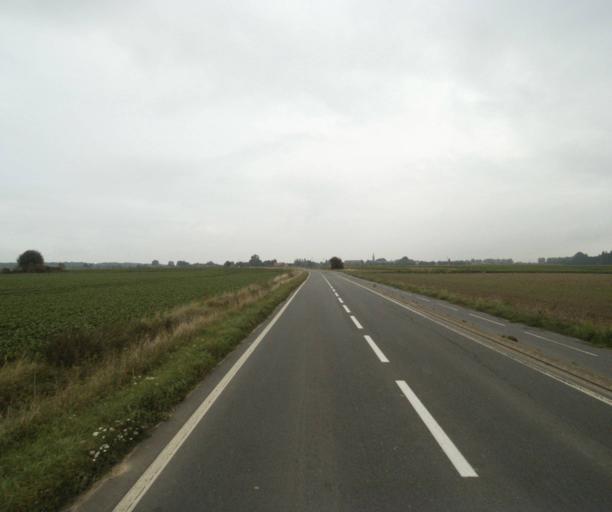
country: FR
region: Nord-Pas-de-Calais
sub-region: Departement du Nord
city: Radinghem-en-Weppes
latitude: 50.5987
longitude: 2.9048
